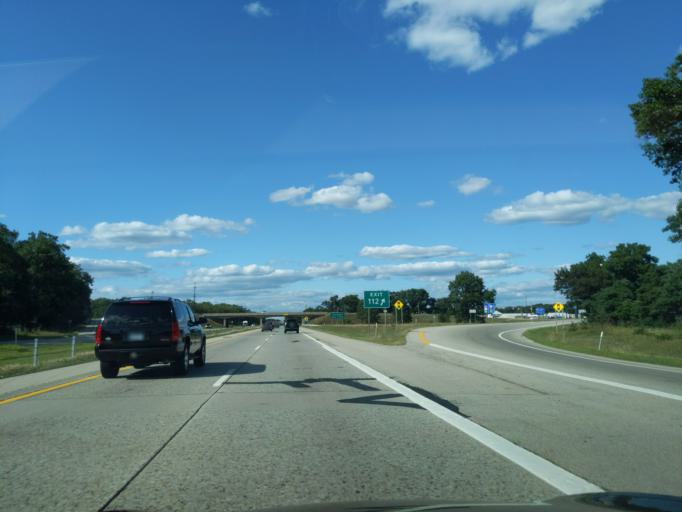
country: US
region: Michigan
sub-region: Muskegon County
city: Muskegon Heights
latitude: 43.2024
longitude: -86.2050
